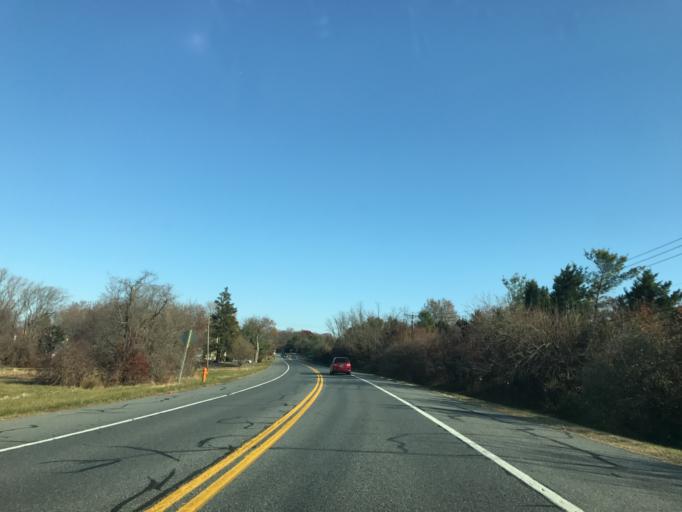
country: US
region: Maryland
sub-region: Howard County
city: Columbia
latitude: 39.2272
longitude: -76.8018
